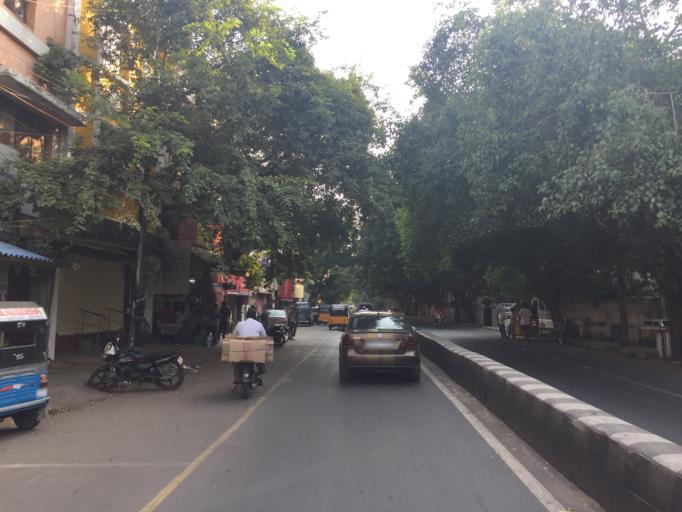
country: IN
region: Tamil Nadu
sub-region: Chennai
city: Gandhi Nagar
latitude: 13.0238
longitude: 80.2643
